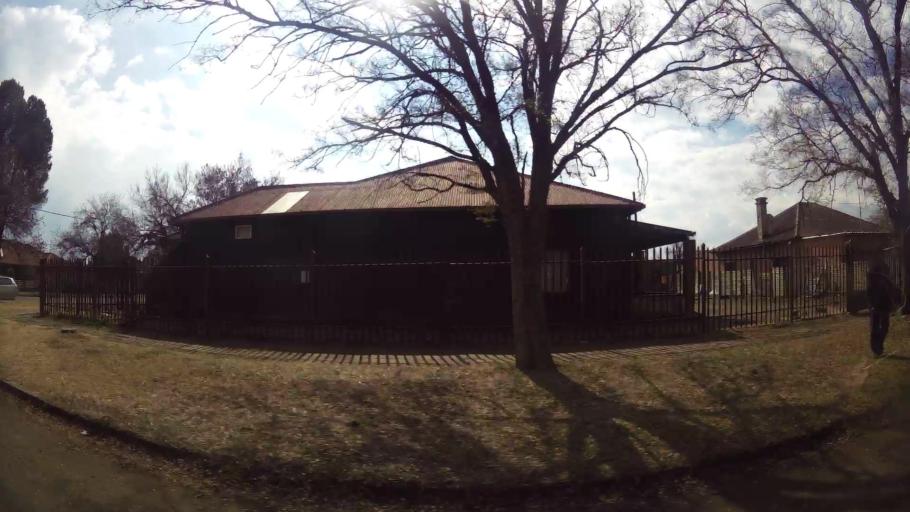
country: ZA
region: Gauteng
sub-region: Sedibeng District Municipality
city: Vereeniging
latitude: -26.6677
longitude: 27.9224
